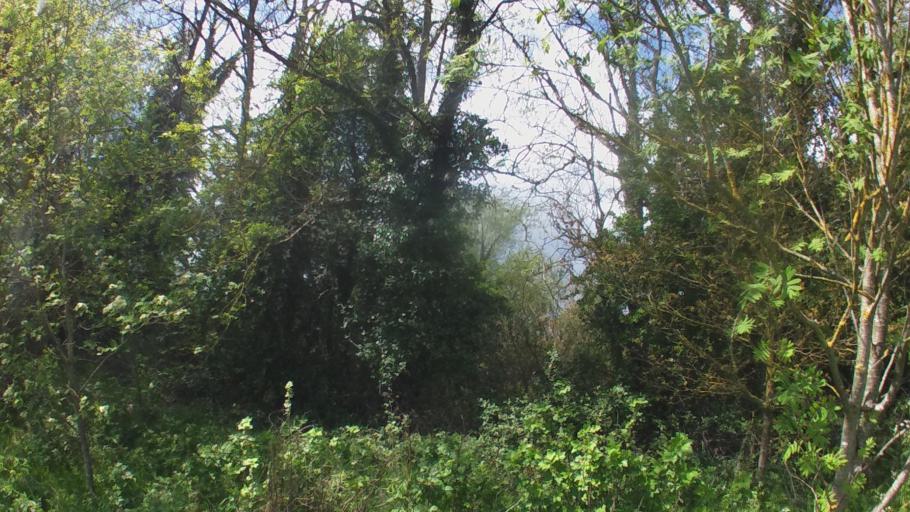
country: IE
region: Leinster
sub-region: Kilkenny
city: Thomastown
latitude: 52.5948
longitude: -7.1851
